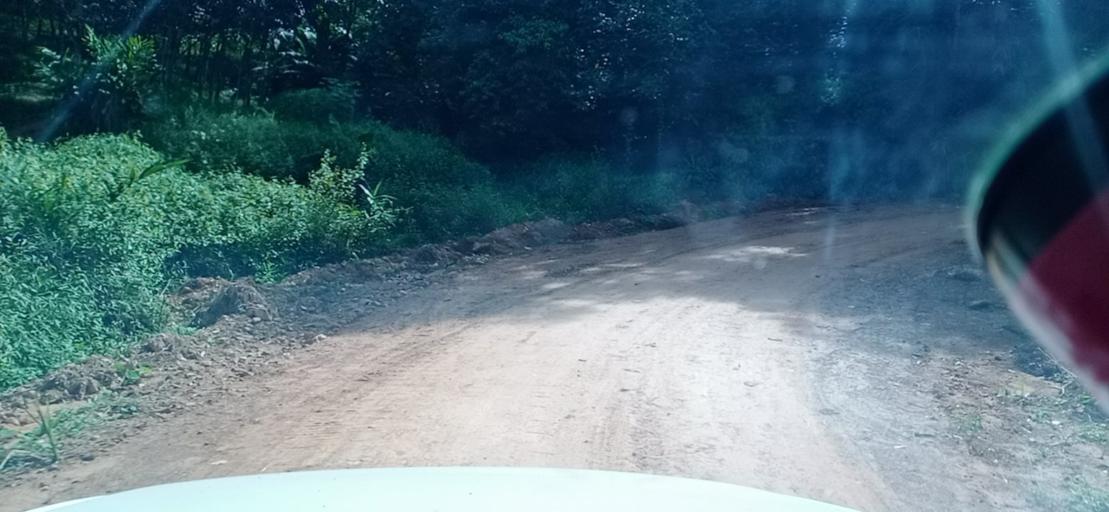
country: TH
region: Changwat Bueng Kan
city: Pak Khat
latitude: 18.6379
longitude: 103.2590
